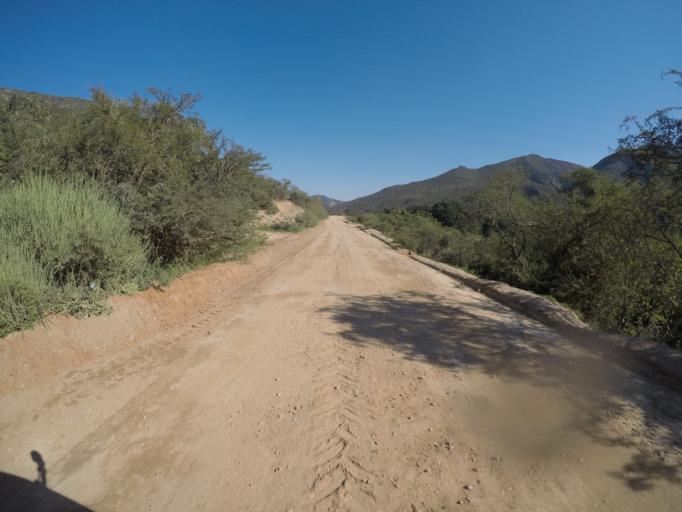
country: ZA
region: Eastern Cape
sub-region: Cacadu District Municipality
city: Kruisfontein
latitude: -33.6637
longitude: 24.5578
